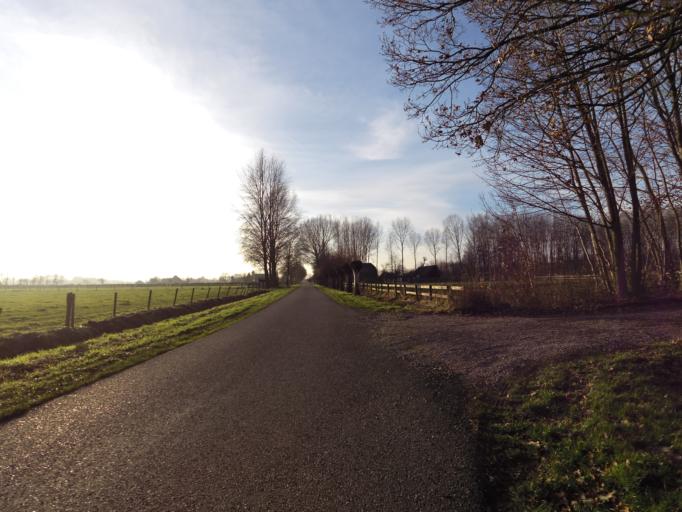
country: NL
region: Gelderland
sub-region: Gemeente Doesburg
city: Doesburg
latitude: 51.9606
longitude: 6.1531
